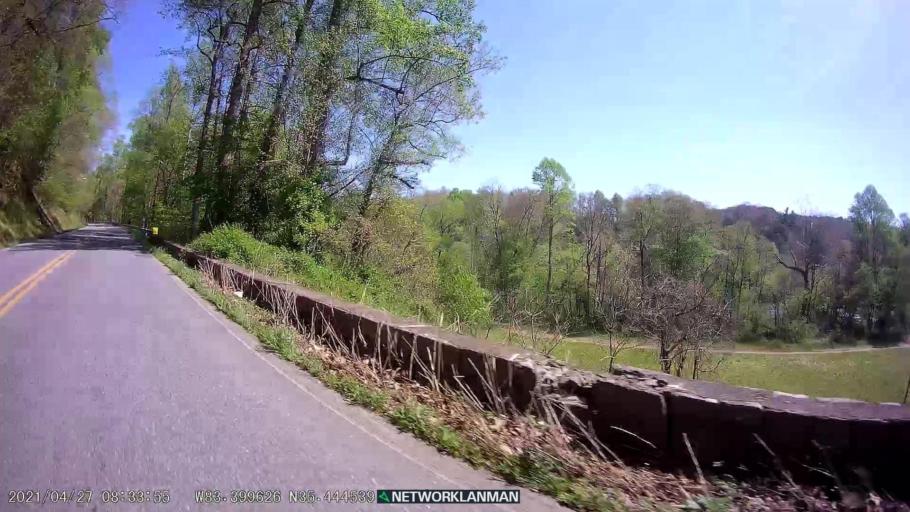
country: US
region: North Carolina
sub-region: Swain County
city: Bryson City
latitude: 35.4448
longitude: -83.3997
